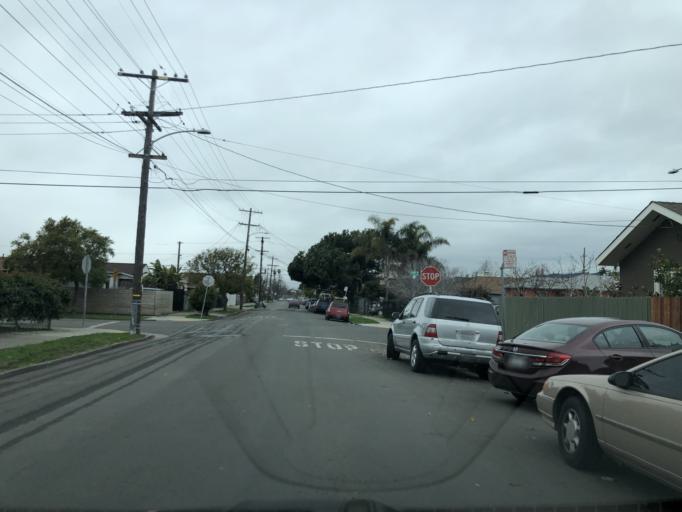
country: US
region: California
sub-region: Alameda County
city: San Leandro
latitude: 37.7485
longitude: -122.1782
